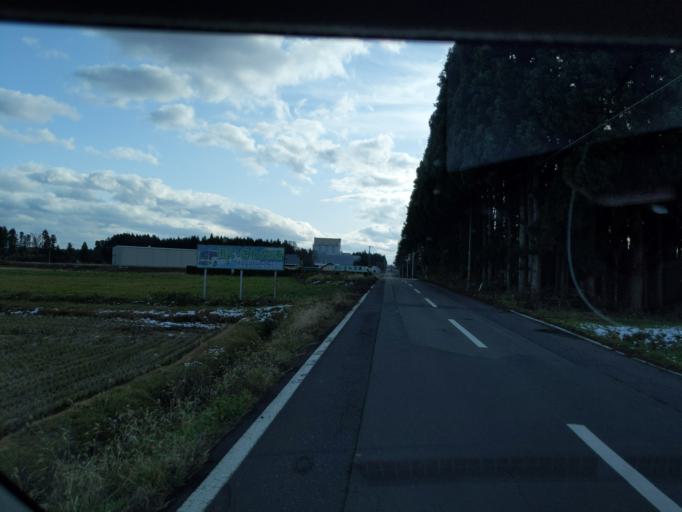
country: JP
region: Iwate
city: Mizusawa
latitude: 39.1088
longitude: 141.0821
